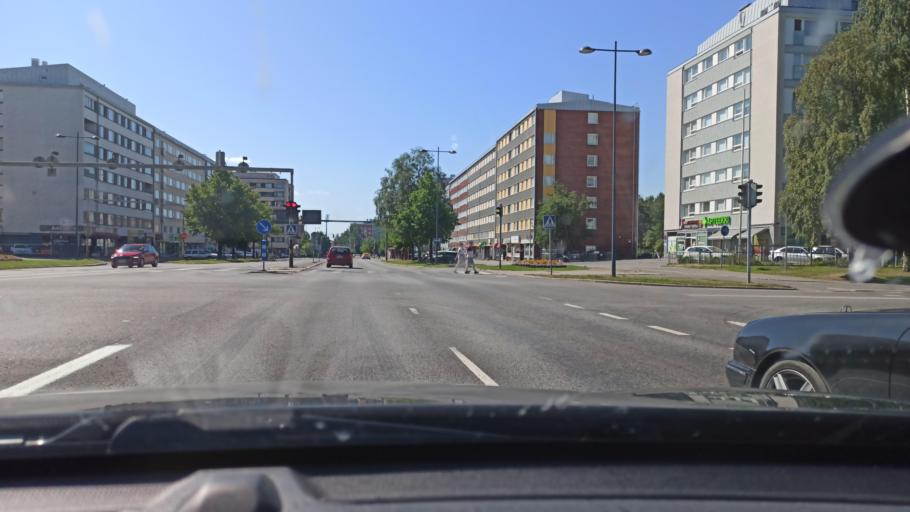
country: FI
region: Northern Ostrobothnia
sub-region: Oulu
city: Oulu
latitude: 65.0263
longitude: 25.4708
